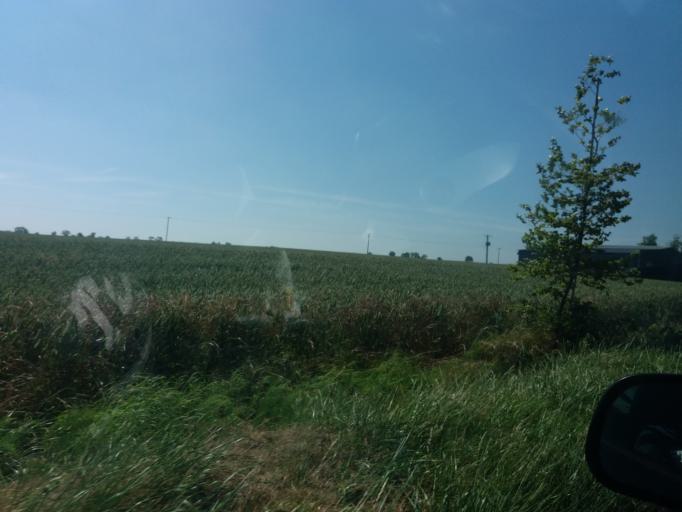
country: IE
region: Leinster
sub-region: Fingal County
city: Swords
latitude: 53.5221
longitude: -6.2844
